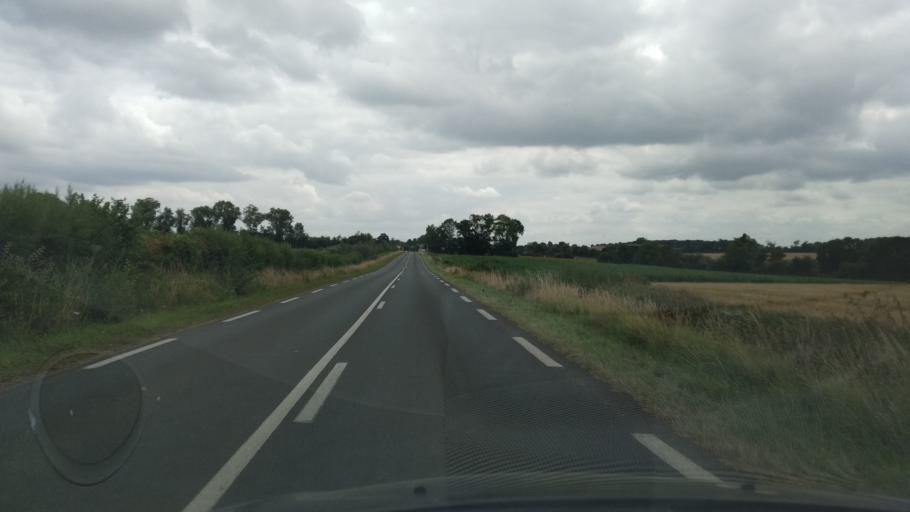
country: FR
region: Poitou-Charentes
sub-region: Departement de la Vienne
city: La Villedieu-du-Clain
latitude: 46.4655
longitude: 0.3675
